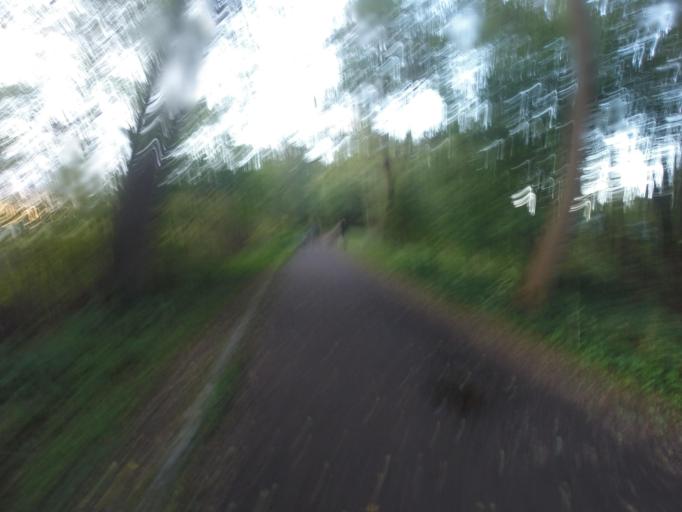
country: DK
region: Capital Region
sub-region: Gladsaxe Municipality
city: Buddinge
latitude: 55.7680
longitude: 12.4712
